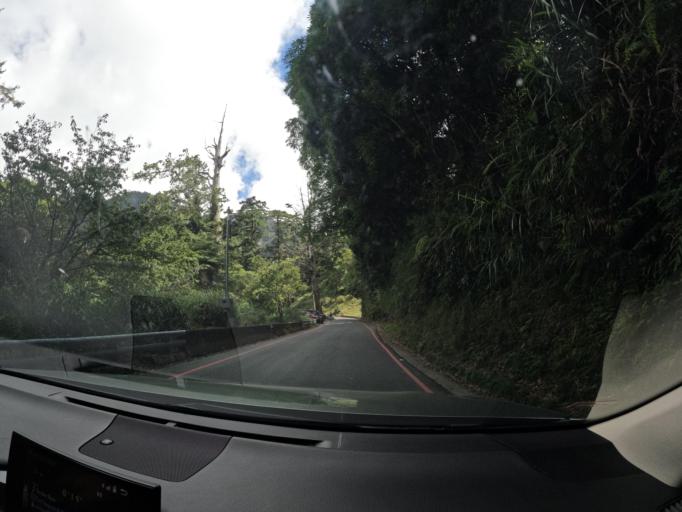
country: TW
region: Taiwan
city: Yujing
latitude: 23.2662
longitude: 120.9395
